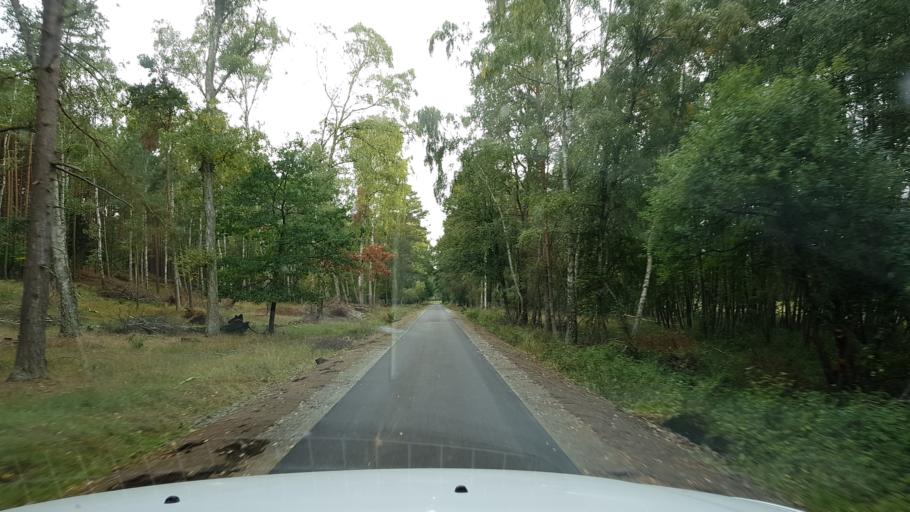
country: PL
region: West Pomeranian Voivodeship
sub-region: Powiat gryfinski
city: Cedynia
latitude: 52.8368
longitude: 14.2685
